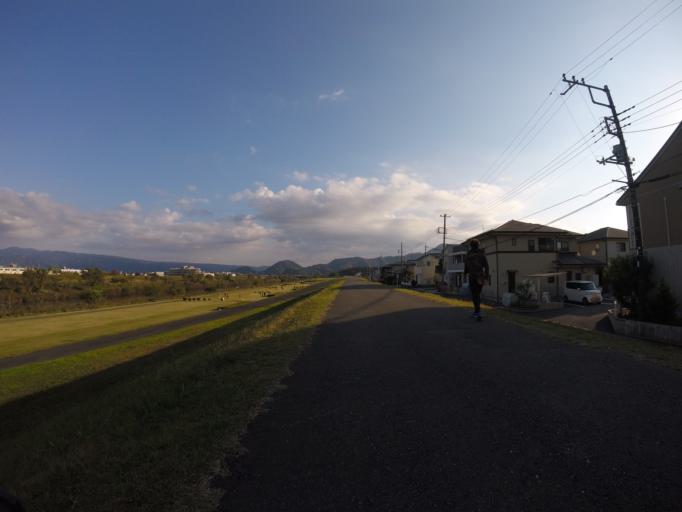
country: JP
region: Shizuoka
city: Mishima
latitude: 35.0898
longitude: 138.9022
